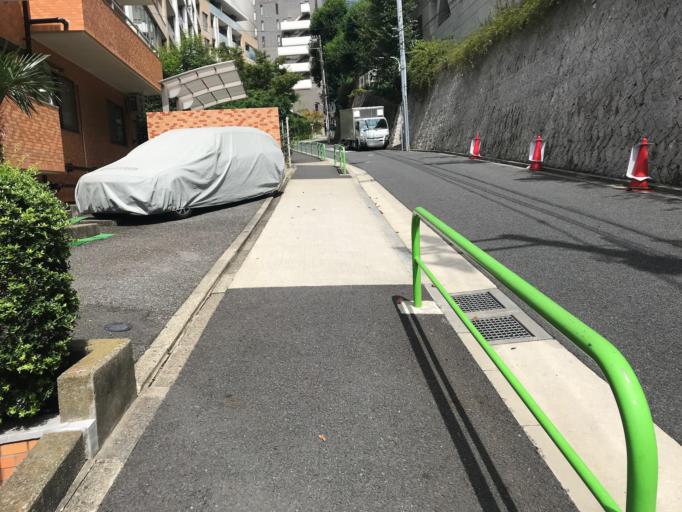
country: JP
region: Tokyo
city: Tokyo
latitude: 35.6588
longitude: 139.7400
